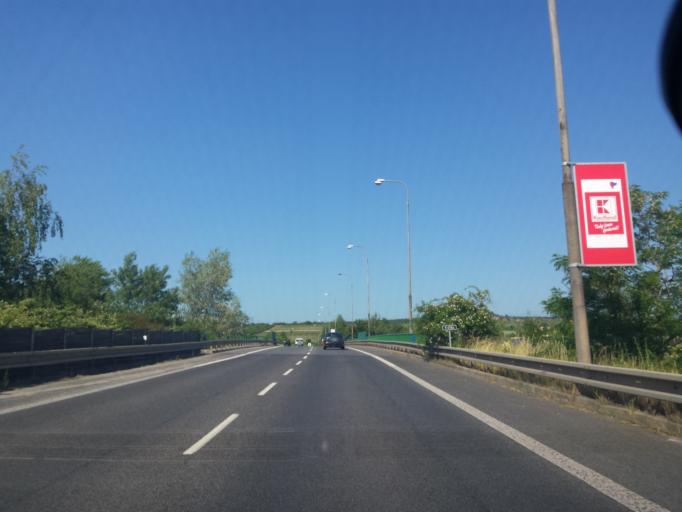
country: CZ
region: Central Bohemia
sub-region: Okres Melnik
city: Melnik
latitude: 50.3649
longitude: 14.4743
